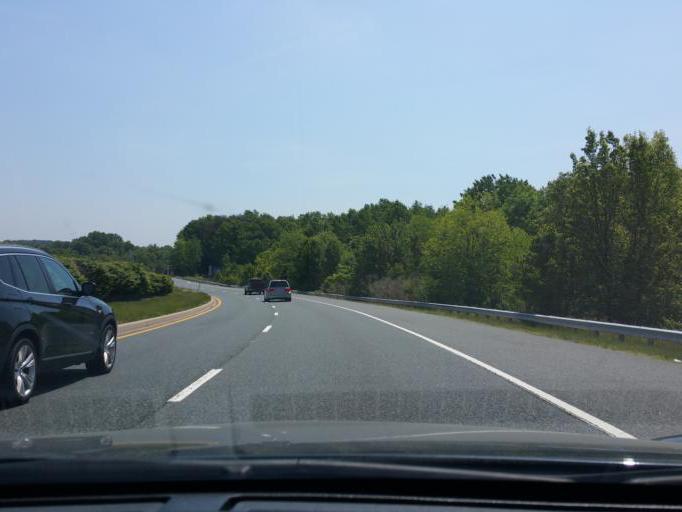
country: US
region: Maryland
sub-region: Baltimore County
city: Carney
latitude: 39.3808
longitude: -76.5166
